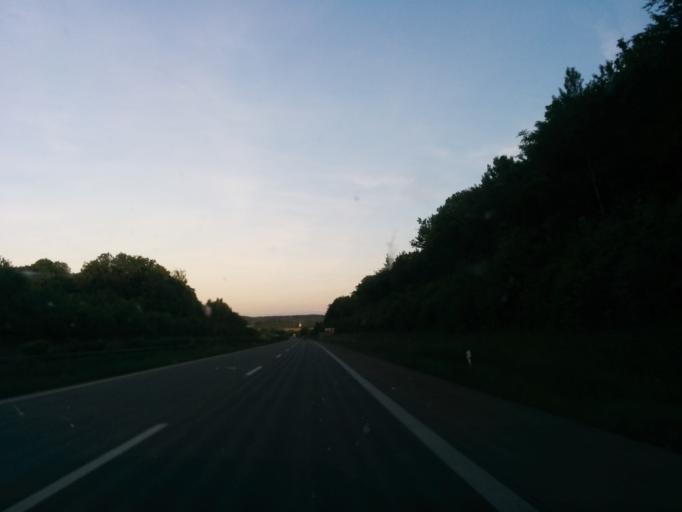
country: DE
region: Bavaria
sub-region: Regierungsbezirk Mittelfranken
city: Ohrenbach
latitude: 49.4677
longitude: 10.2328
